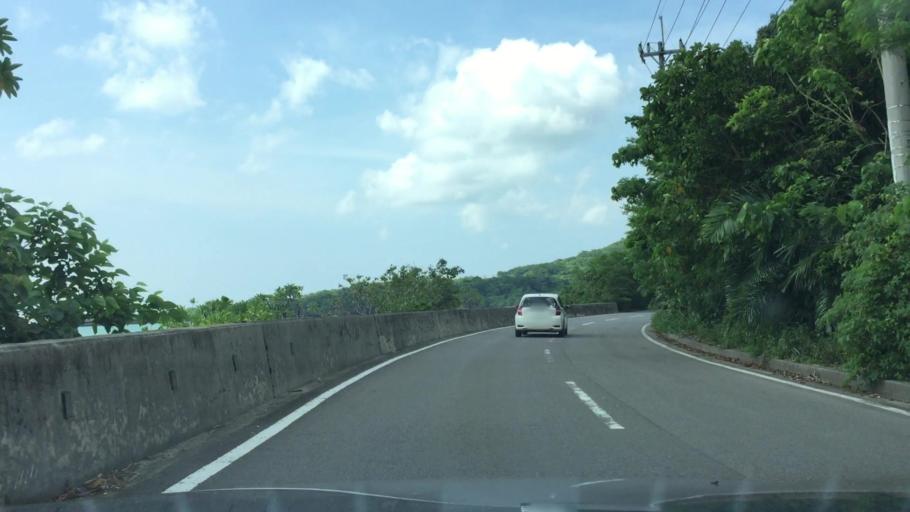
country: JP
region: Okinawa
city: Ishigaki
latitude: 24.4615
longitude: 124.2261
